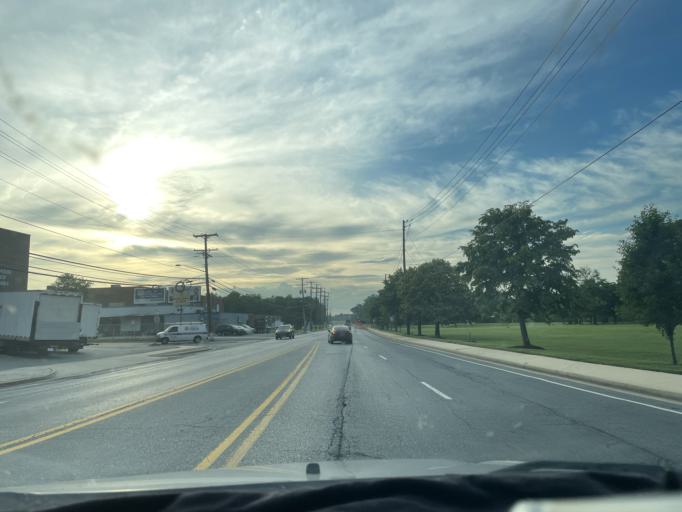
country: US
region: Maryland
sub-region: Prince George's County
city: Beltsville
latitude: 39.0232
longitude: -76.9111
